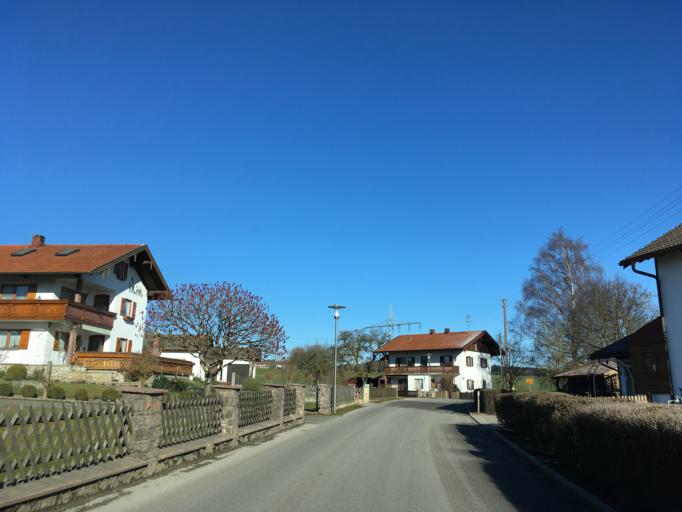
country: DE
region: Bavaria
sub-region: Upper Bavaria
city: Pittenhart
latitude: 47.9877
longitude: 12.3578
